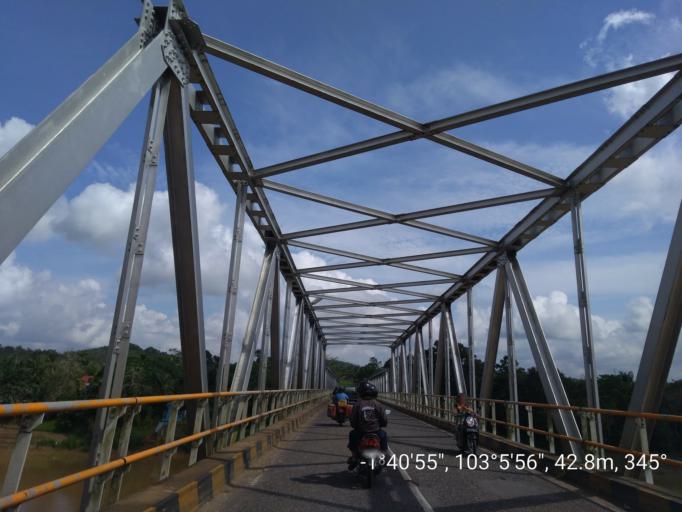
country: ID
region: Jambi
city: Muara Tembesi
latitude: -1.6822
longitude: 103.0991
